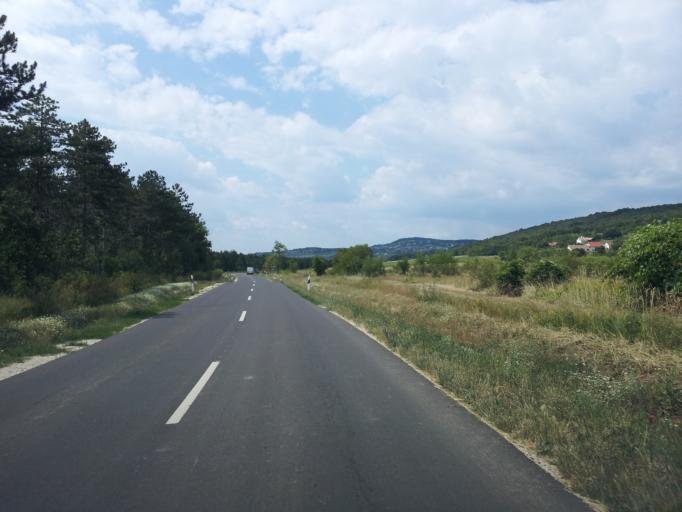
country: HU
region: Veszprem
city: Zanka
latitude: 46.9026
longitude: 17.7369
